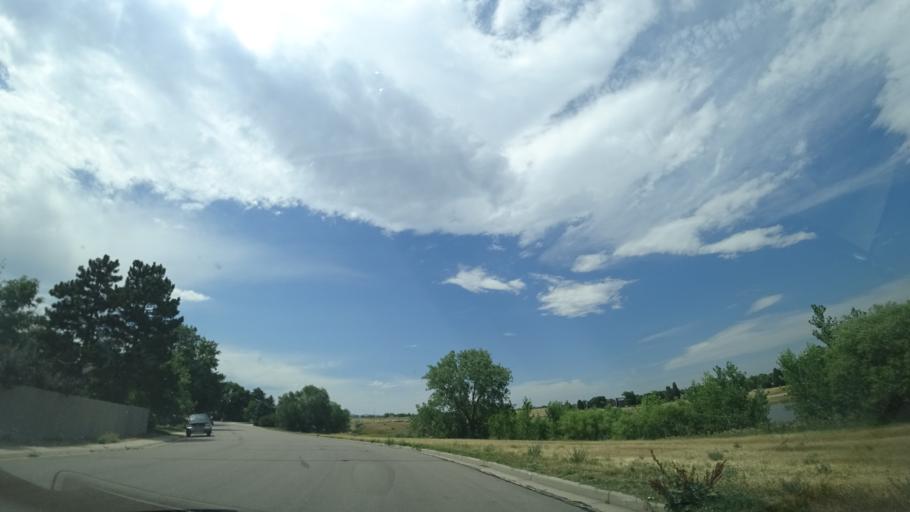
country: US
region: Colorado
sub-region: Jefferson County
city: Lakewood
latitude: 39.6914
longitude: -105.1120
